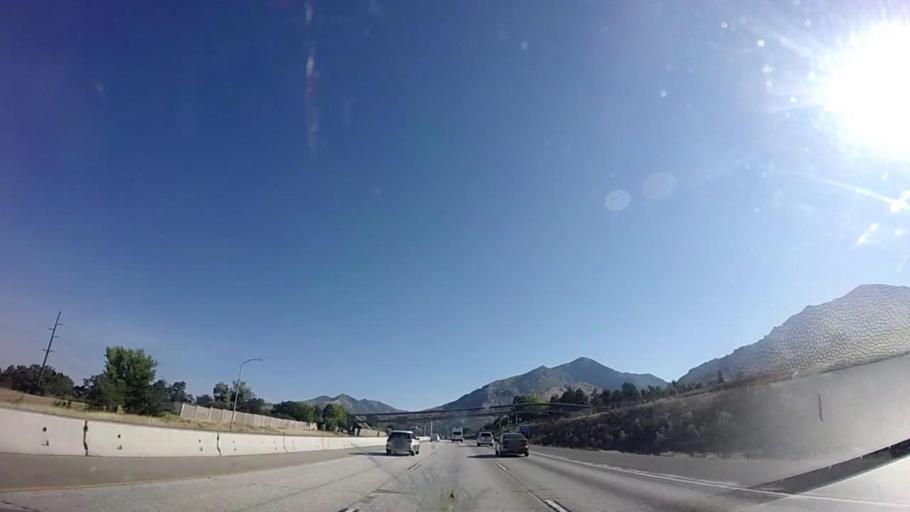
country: US
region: Utah
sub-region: Salt Lake County
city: Mount Olympus
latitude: 40.6773
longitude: -111.8003
